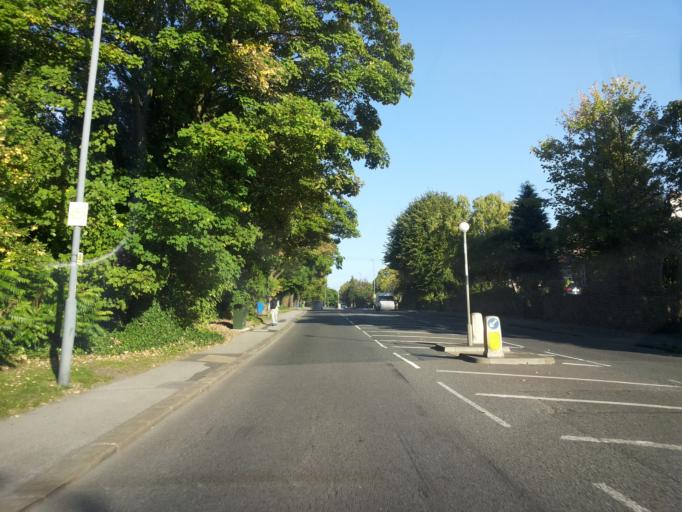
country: GB
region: England
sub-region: Derbyshire
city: Wingerworth
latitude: 53.2314
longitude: -1.4796
